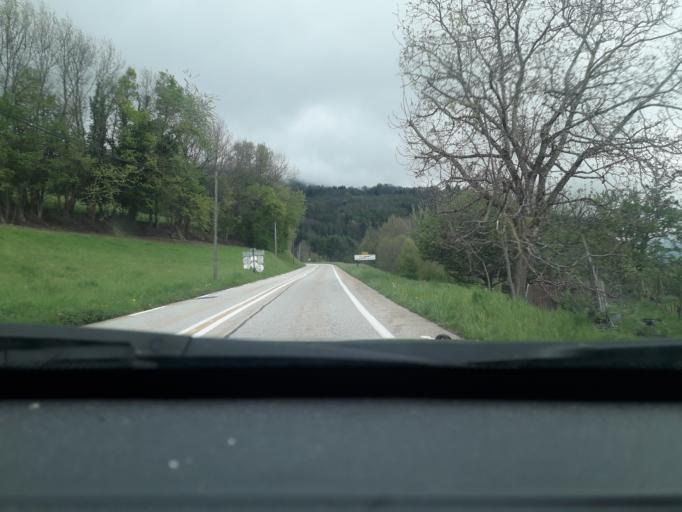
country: FR
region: Rhone-Alpes
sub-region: Departement de l'Isere
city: Vaulnaveys-le-Bas
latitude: 45.1161
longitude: 5.8288
